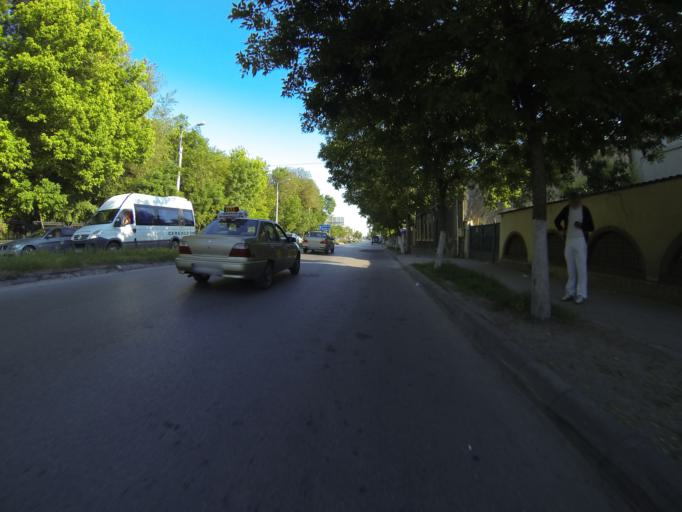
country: RO
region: Dolj
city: Craiova
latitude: 44.2999
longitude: 23.7988
